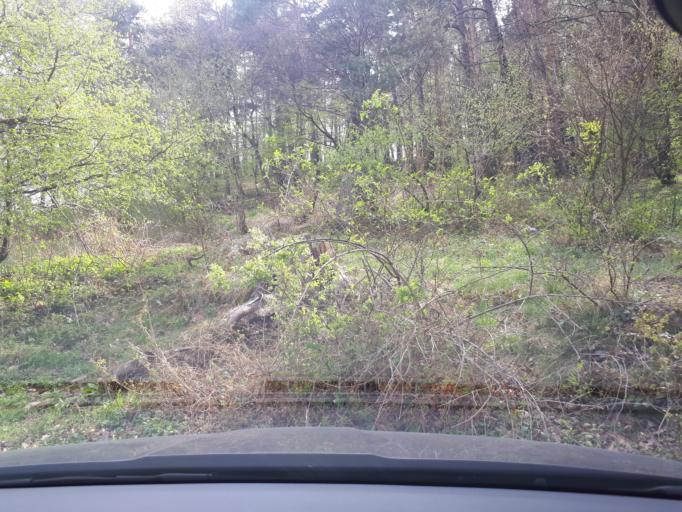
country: RO
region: Brasov
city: Codlea
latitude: 45.7061
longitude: 25.4354
